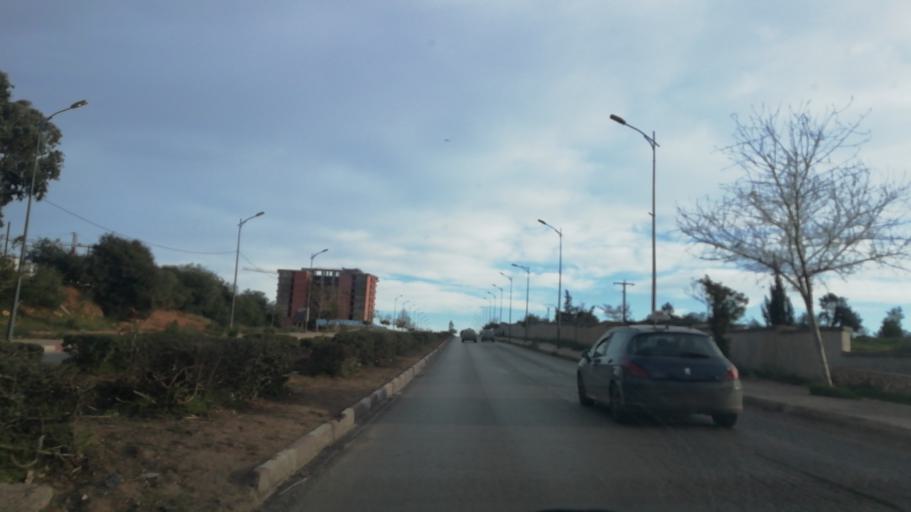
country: DZ
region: Oran
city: Bir el Djir
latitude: 35.7102
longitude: -0.5747
